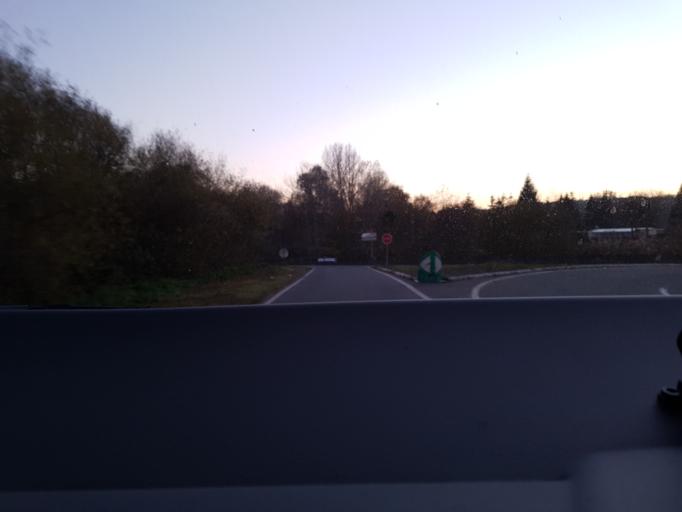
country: FR
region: Nord-Pas-de-Calais
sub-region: Departement du Nord
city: Watten
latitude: 50.8415
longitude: 2.2061
